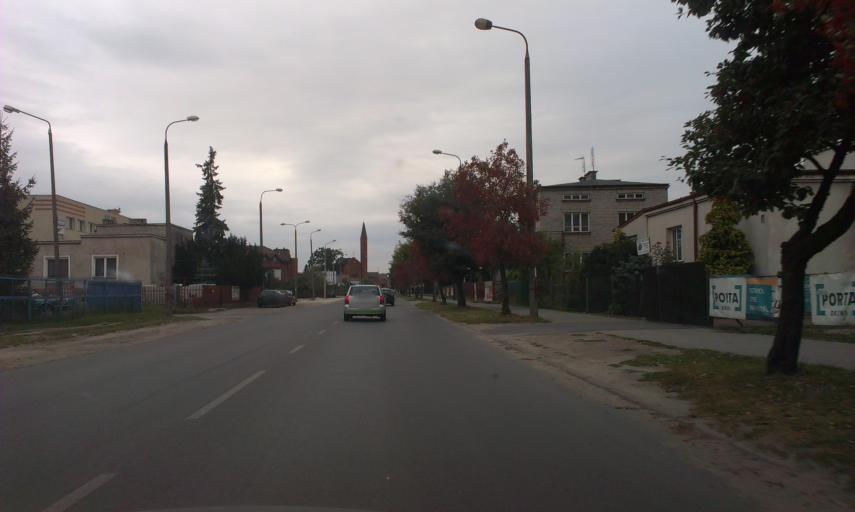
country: PL
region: Masovian Voivodeship
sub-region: Radom
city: Radom
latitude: 51.4097
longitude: 21.1393
